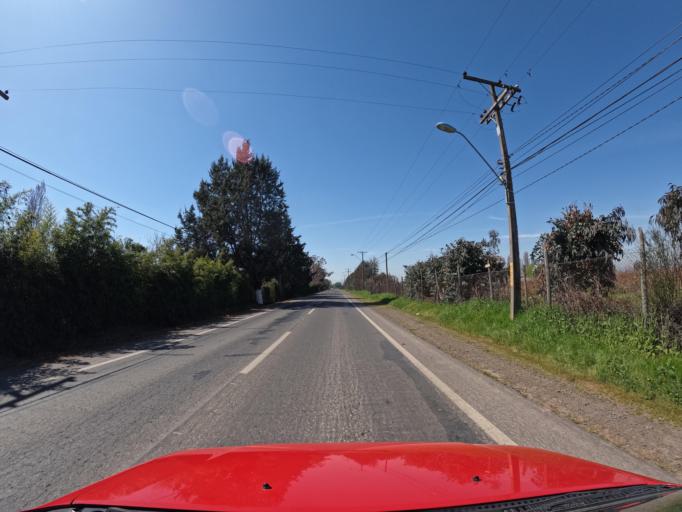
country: CL
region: Maule
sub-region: Provincia de Curico
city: Rauco
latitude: -34.9963
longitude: -71.3637
